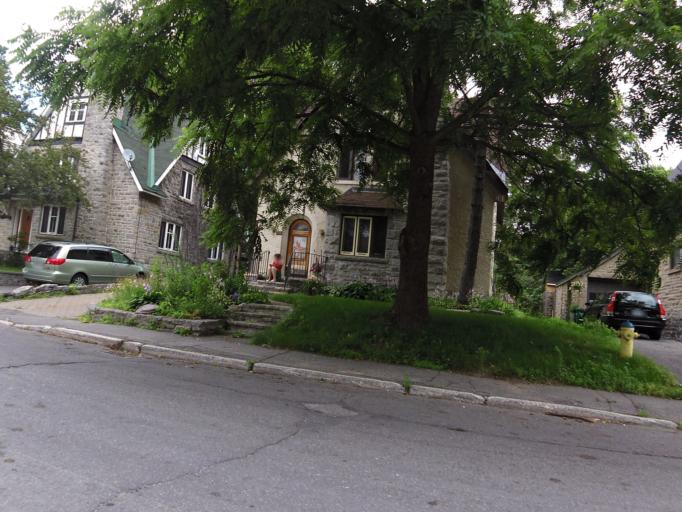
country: CA
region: Ontario
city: Ottawa
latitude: 45.3935
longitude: -75.7192
